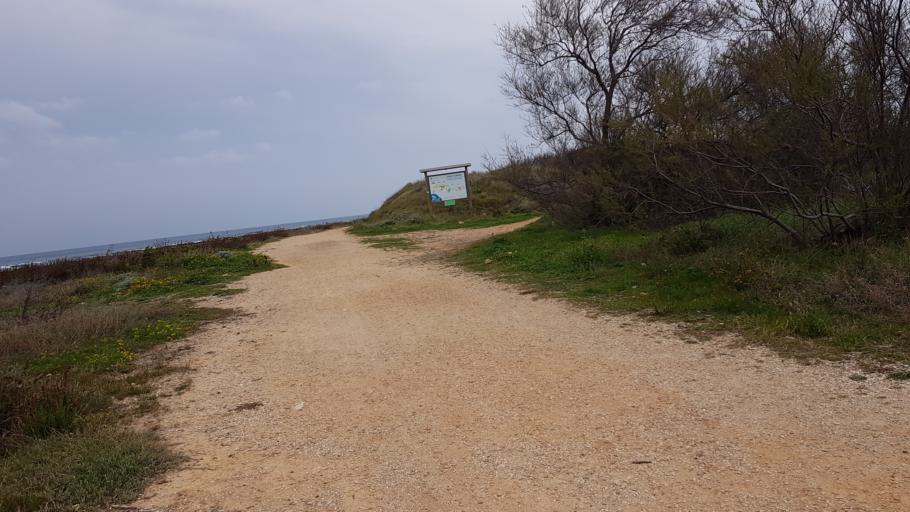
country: IT
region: Apulia
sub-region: Provincia di Brindisi
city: Materdomini
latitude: 40.6766
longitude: 17.9448
